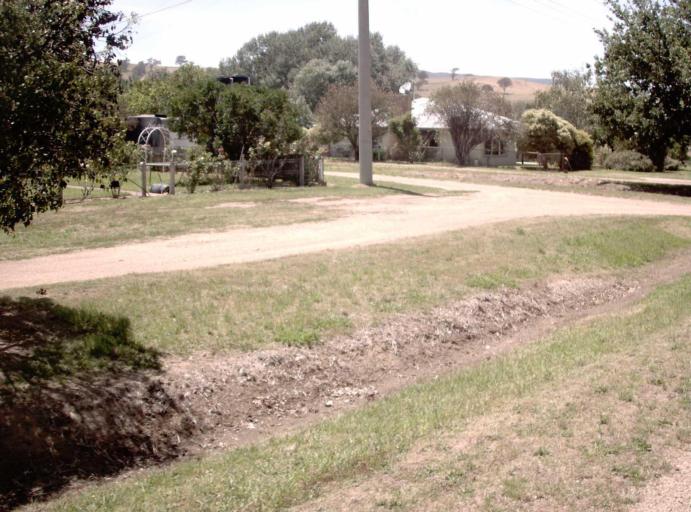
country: AU
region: Victoria
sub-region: East Gippsland
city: Bairnsdale
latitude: -37.2589
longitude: 147.7145
